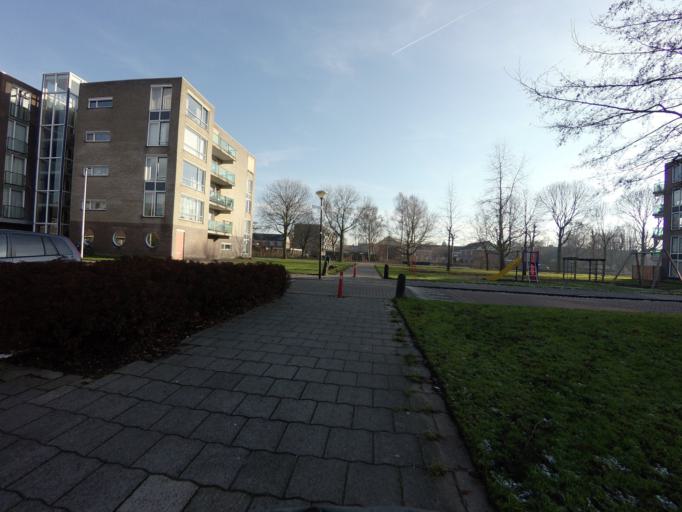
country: NL
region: Utrecht
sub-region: Gemeente De Ronde Venen
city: Mijdrecht
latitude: 52.2064
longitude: 4.8545
